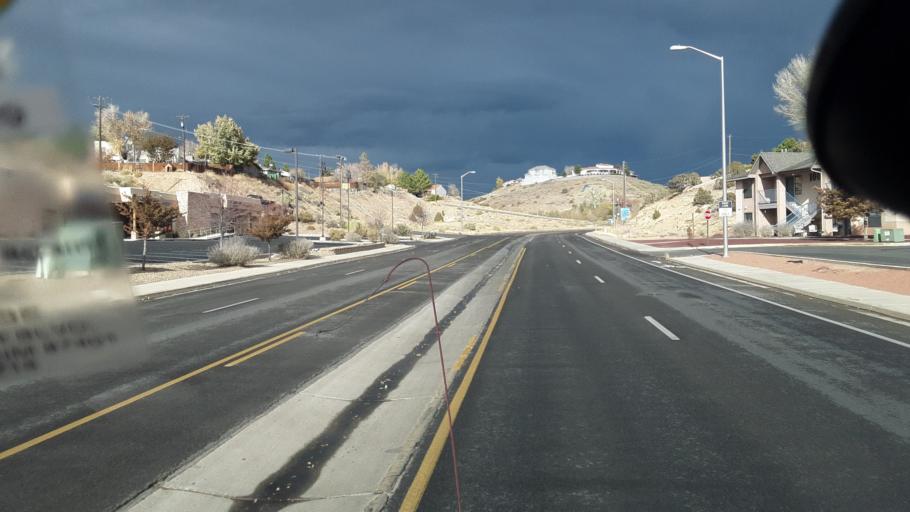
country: US
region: New Mexico
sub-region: San Juan County
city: Farmington
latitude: 36.7599
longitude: -108.1946
